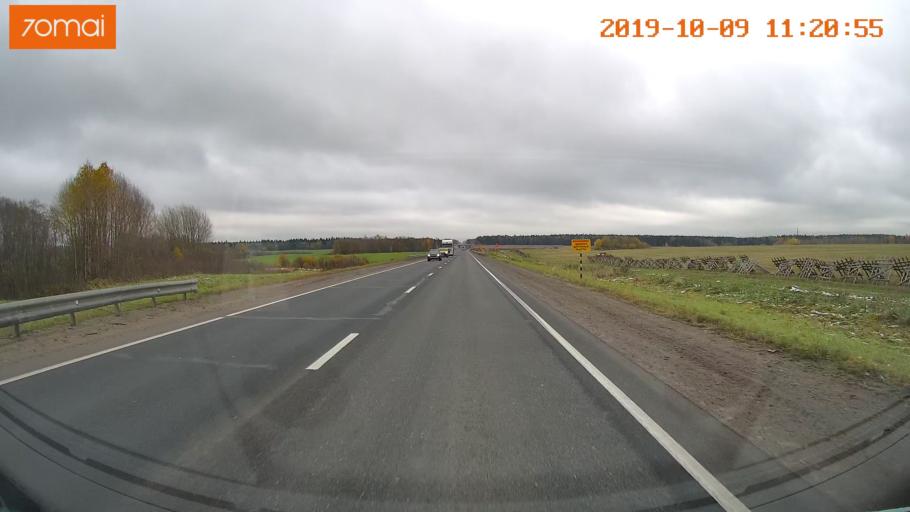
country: RU
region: Vologda
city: Vologda
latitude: 59.1442
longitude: 39.9444
